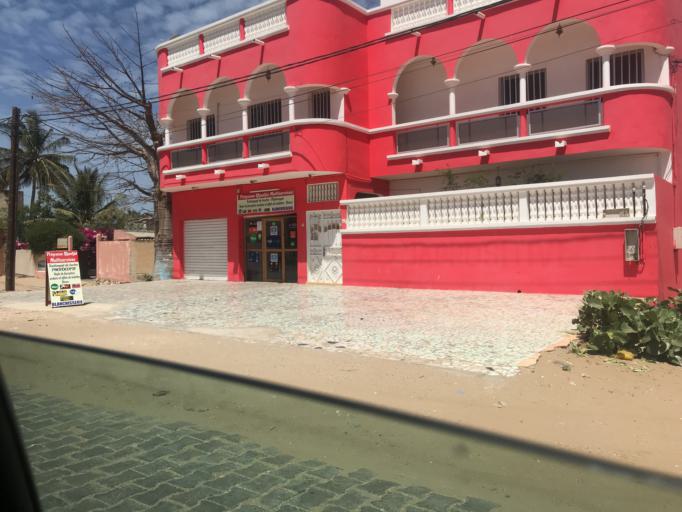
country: SN
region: Saint-Louis
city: Saint-Louis
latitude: 16.0340
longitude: -16.4701
